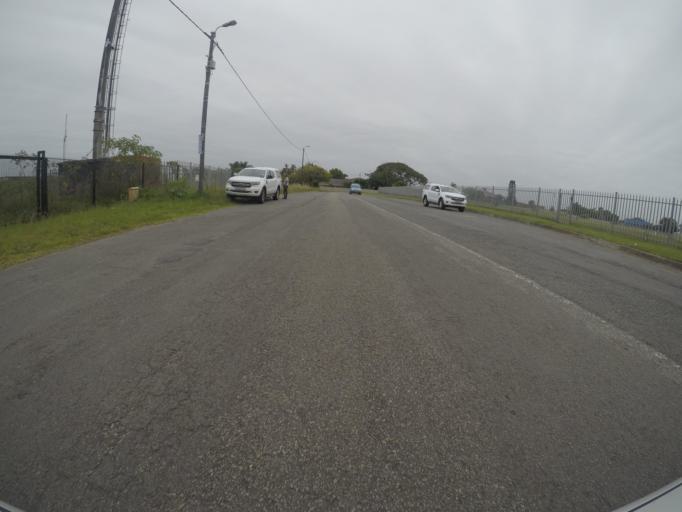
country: ZA
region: Eastern Cape
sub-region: Buffalo City Metropolitan Municipality
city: East London
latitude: -32.9672
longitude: 27.9345
